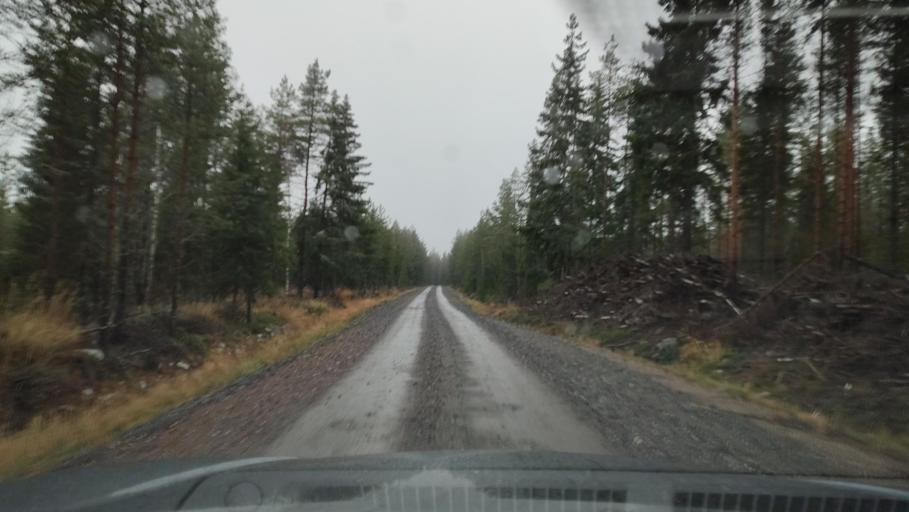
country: FI
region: Southern Ostrobothnia
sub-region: Suupohja
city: Karijoki
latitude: 62.1751
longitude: 21.7006
